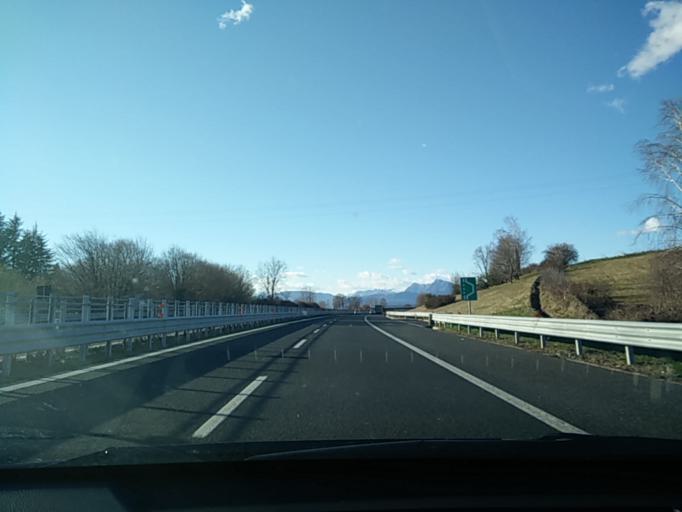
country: IT
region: Friuli Venezia Giulia
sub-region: Provincia di Udine
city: Pagnacco
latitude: 46.1365
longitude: 13.1812
